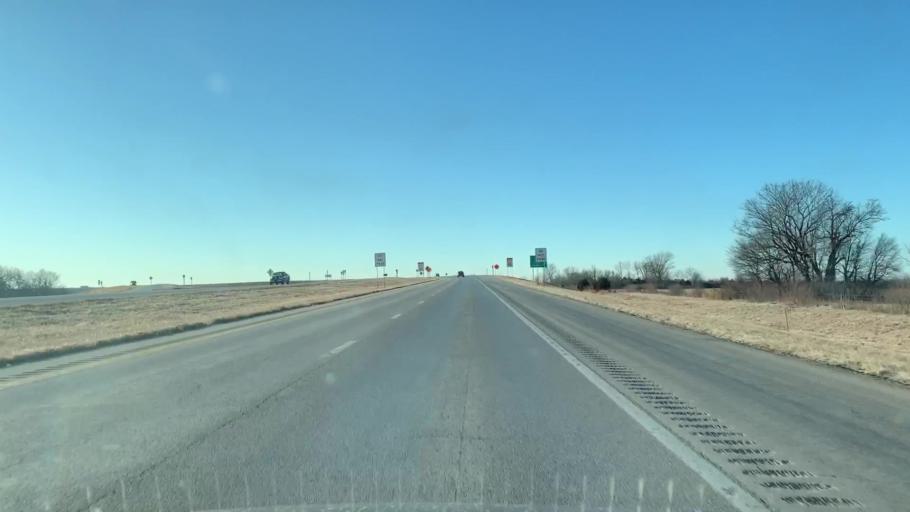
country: US
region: Kansas
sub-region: Bourbon County
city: Fort Scott
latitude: 37.7737
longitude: -94.7060
